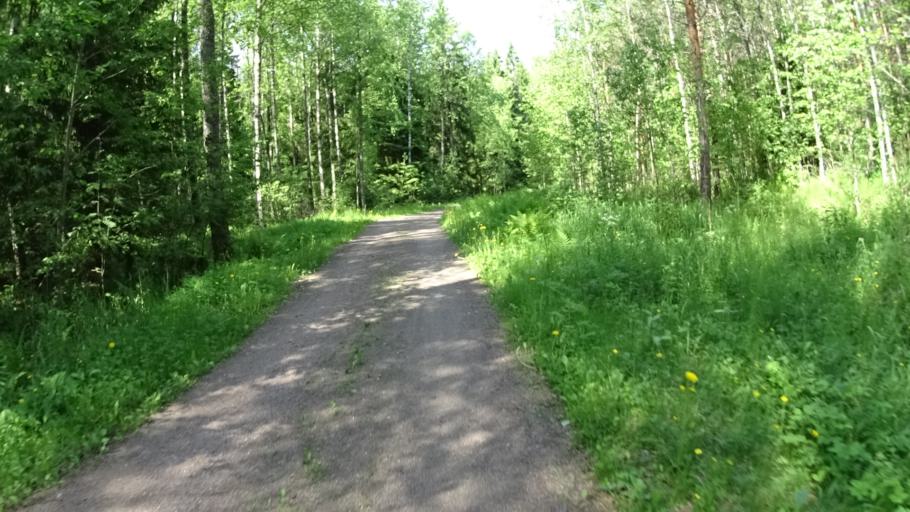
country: FI
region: Uusimaa
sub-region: Helsinki
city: Kilo
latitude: 60.3235
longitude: 24.7568
